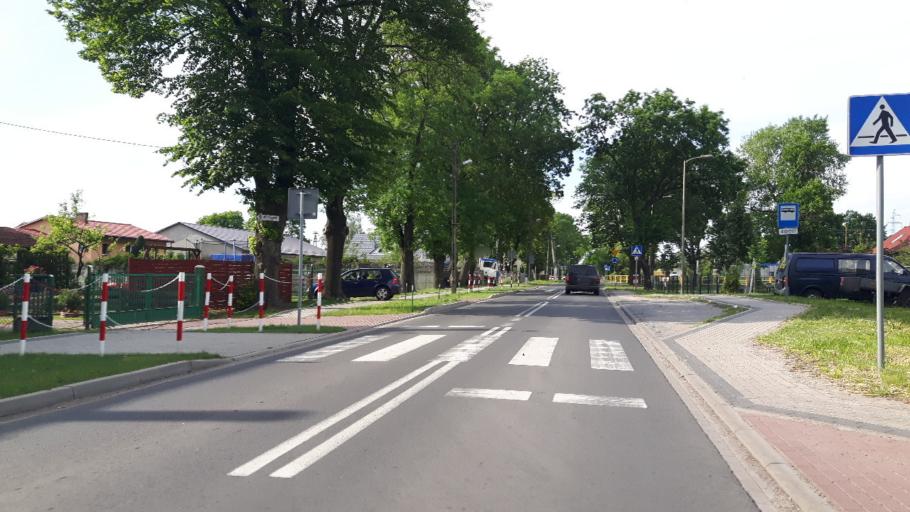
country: PL
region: West Pomeranian Voivodeship
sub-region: Powiat goleniowski
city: Goleniow
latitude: 53.4612
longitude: 14.7726
